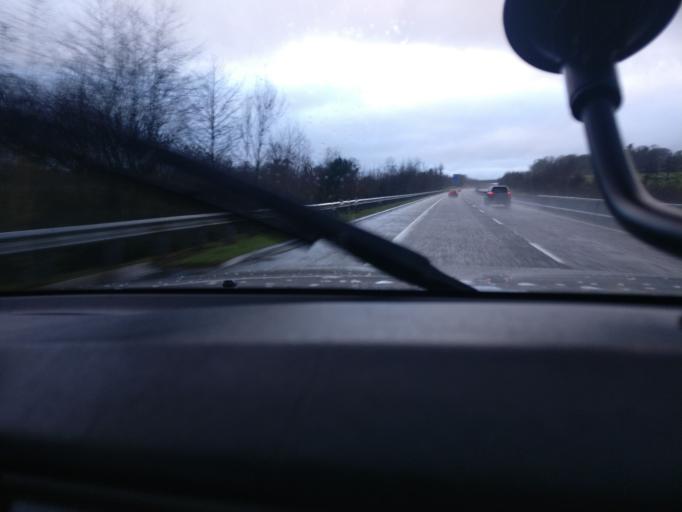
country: IE
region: Leinster
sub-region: An Iarmhi
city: Moate
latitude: 53.3889
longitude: -7.7590
